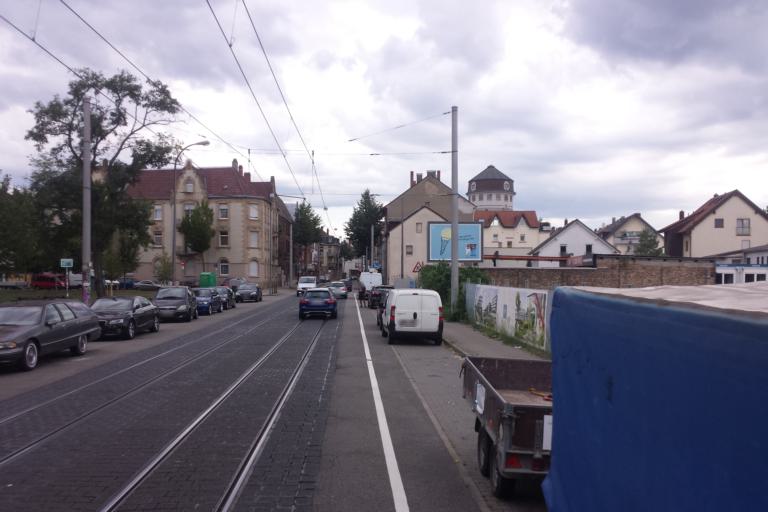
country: DE
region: Baden-Wuerttemberg
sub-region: Karlsruhe Region
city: Mannheim
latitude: 49.5192
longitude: 8.4727
